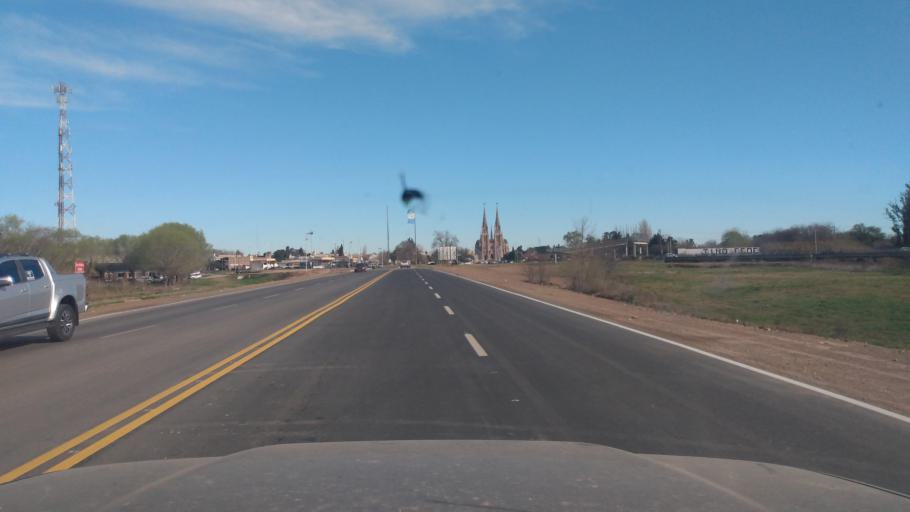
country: AR
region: Buenos Aires
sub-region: Partido de Lujan
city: Lujan
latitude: -34.5530
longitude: -59.1167
